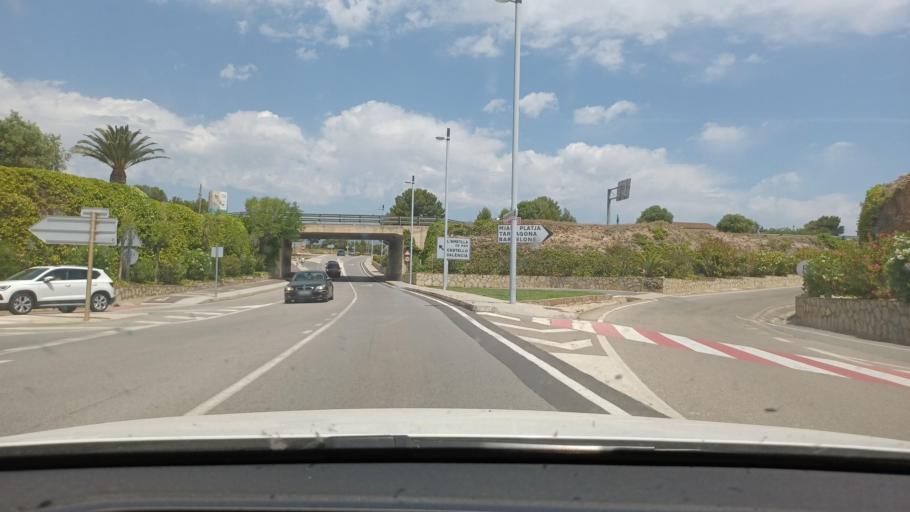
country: ES
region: Catalonia
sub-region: Provincia de Tarragona
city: Colldejou
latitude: 40.9959
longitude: 0.9196
